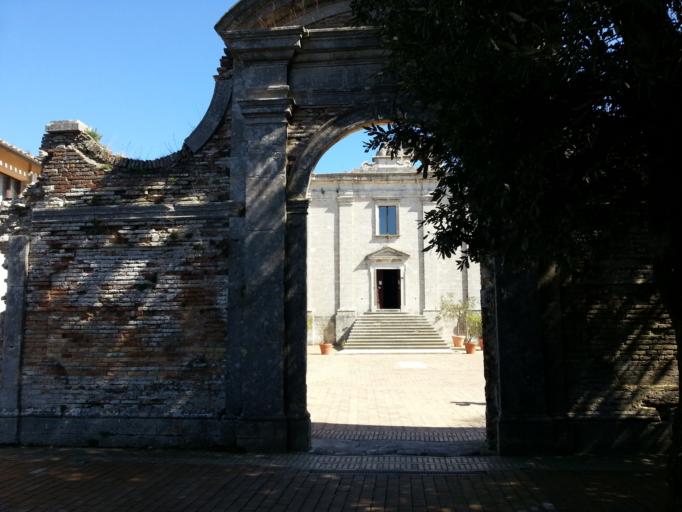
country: IT
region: The Marches
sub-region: Provincia di Ancona
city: Sirolo
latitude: 43.5473
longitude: 13.6161
